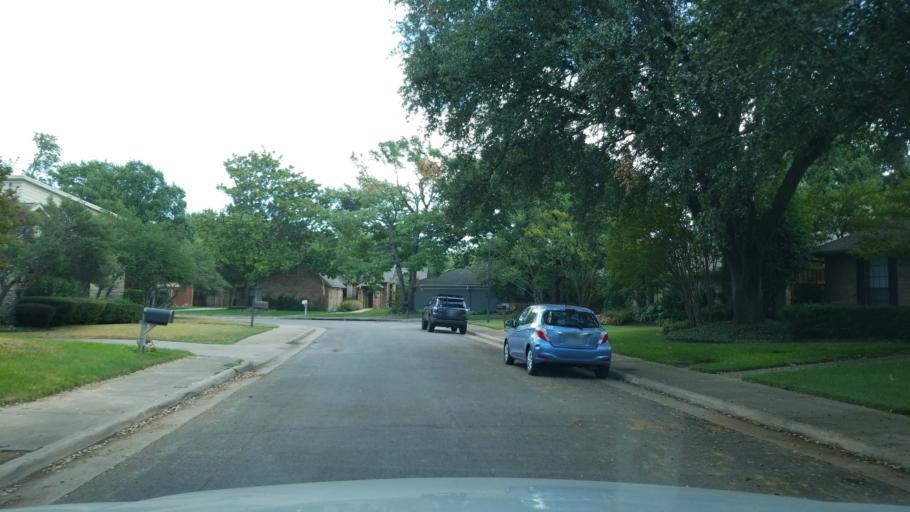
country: US
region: Texas
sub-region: Dallas County
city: Addison
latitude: 32.9682
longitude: -96.7946
